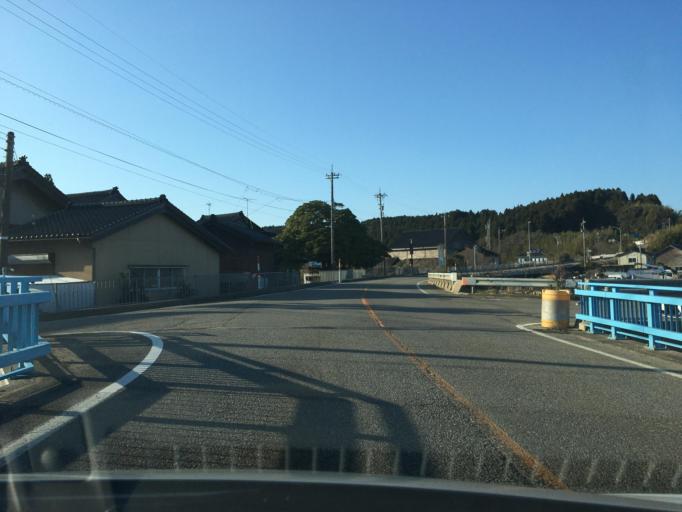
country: JP
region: Ishikawa
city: Nanao
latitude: 36.9769
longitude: 137.0499
